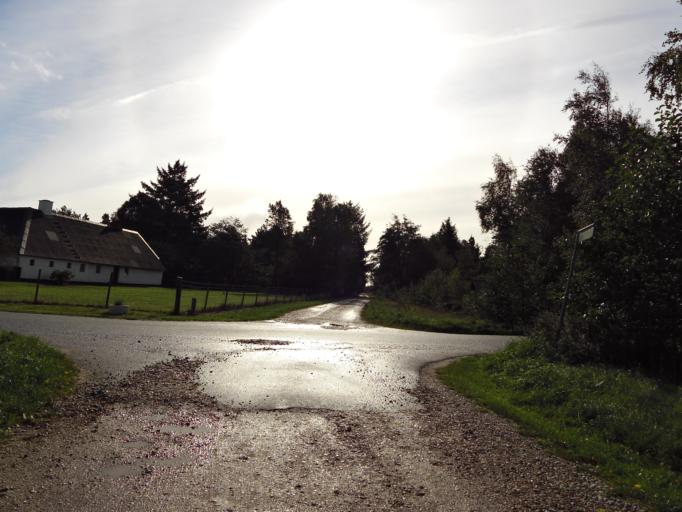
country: DK
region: South Denmark
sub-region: Varde Kommune
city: Oksbol
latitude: 55.5588
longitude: 8.2237
